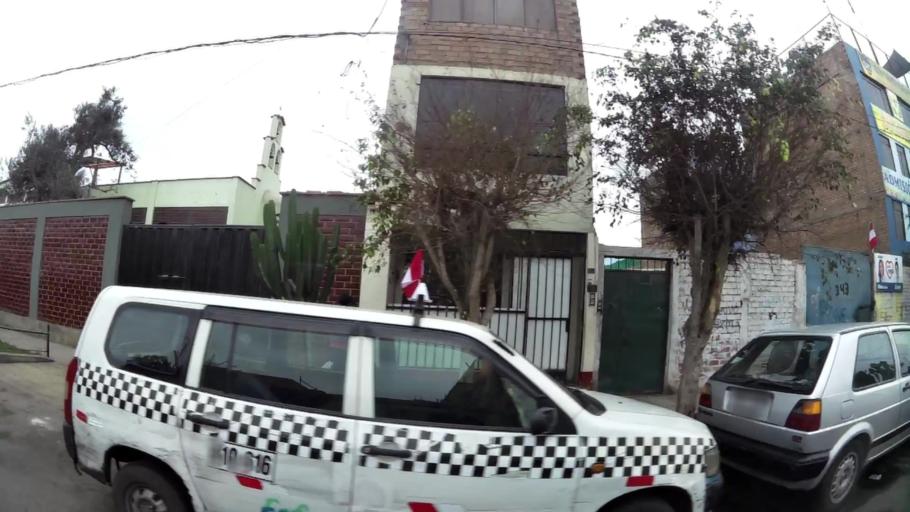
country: PE
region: Lima
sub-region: Lima
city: Surco
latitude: -12.1469
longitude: -77.0031
